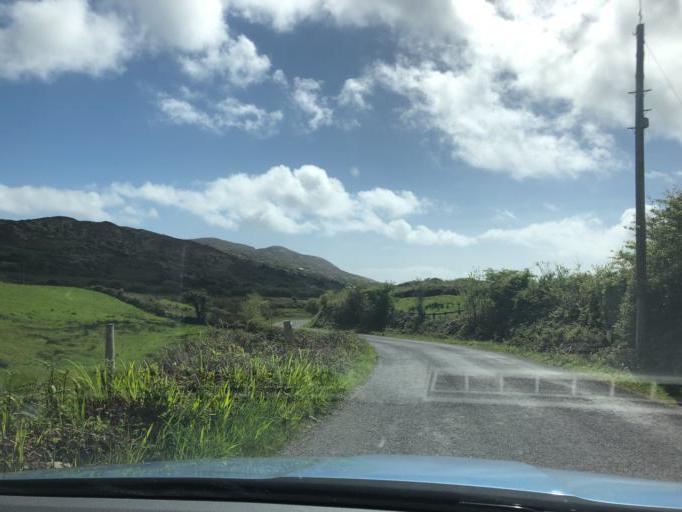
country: IE
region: Munster
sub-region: Ciarrai
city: Cahersiveen
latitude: 51.7678
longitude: -10.1042
